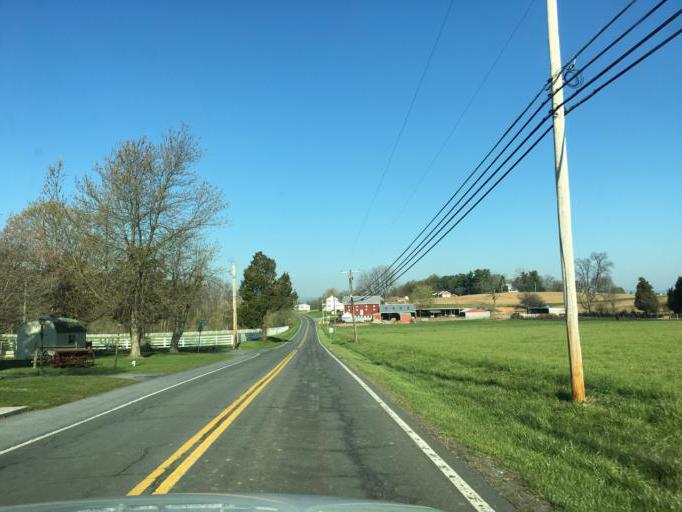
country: US
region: Maryland
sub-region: Frederick County
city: Woodsboro
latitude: 39.4871
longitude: -77.2788
